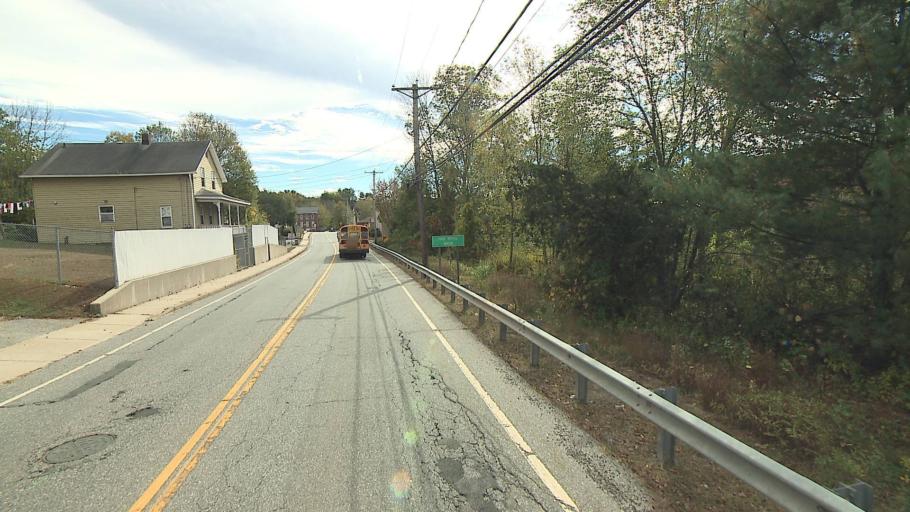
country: US
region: Connecticut
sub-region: Windham County
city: Killingly Center
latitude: 41.8336
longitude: -71.8773
